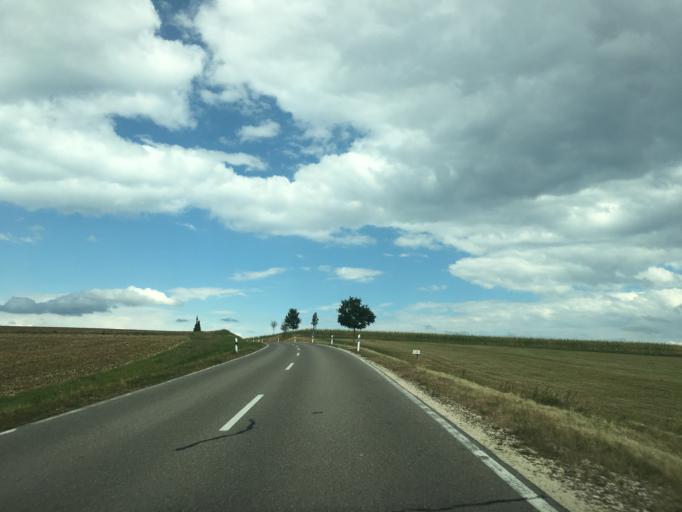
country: DE
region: Baden-Wuerttemberg
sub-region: Tuebingen Region
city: Hayingen
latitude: 48.3135
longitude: 9.4448
